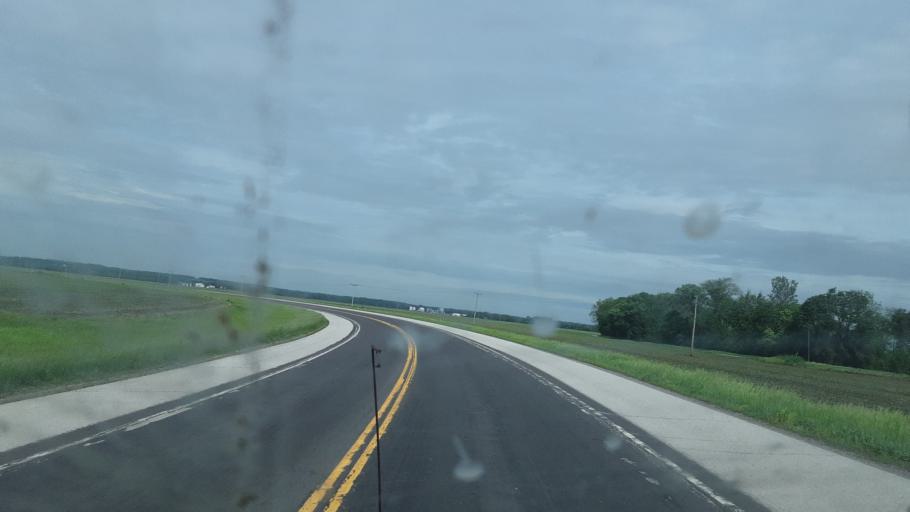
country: US
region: Illinois
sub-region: Hancock County
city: Warsaw
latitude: 40.3930
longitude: -91.5253
